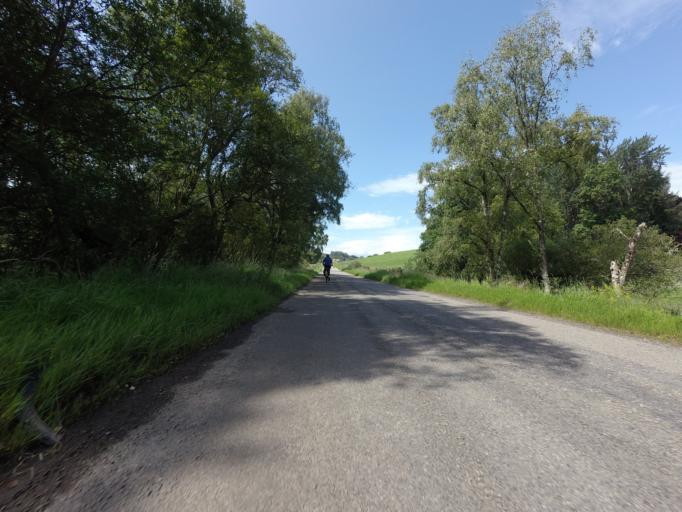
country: GB
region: Scotland
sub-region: Highland
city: Inverness
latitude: 57.5227
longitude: -4.3039
